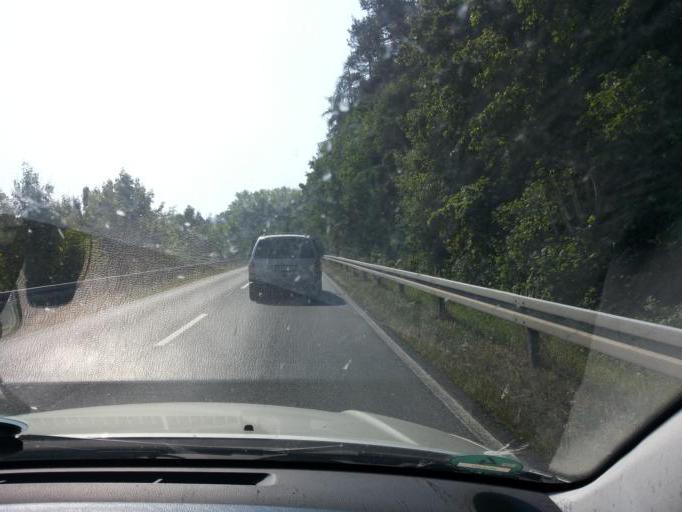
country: DE
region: Bavaria
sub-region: Regierungsbezirk Mittelfranken
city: Ipsheim
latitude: 49.5059
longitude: 10.5026
